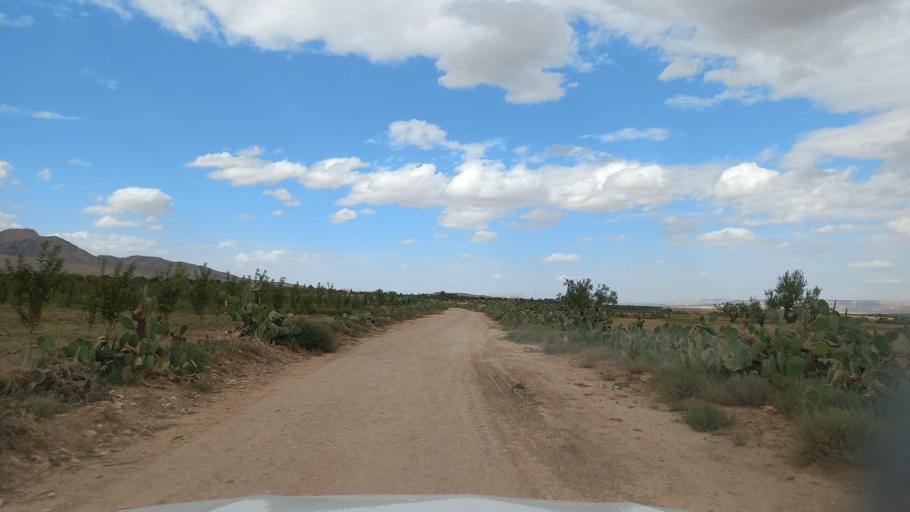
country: TN
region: Al Qasrayn
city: Sbiba
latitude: 35.4330
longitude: 9.0979
